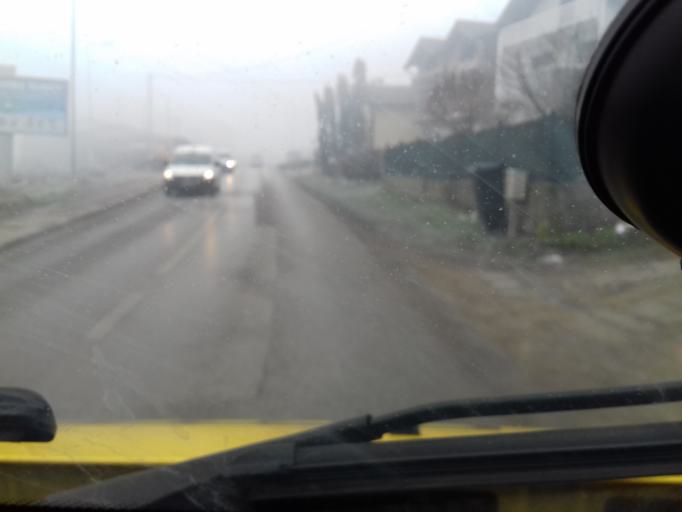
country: BA
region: Federation of Bosnia and Herzegovina
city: Visoko
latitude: 43.9965
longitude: 18.1672
